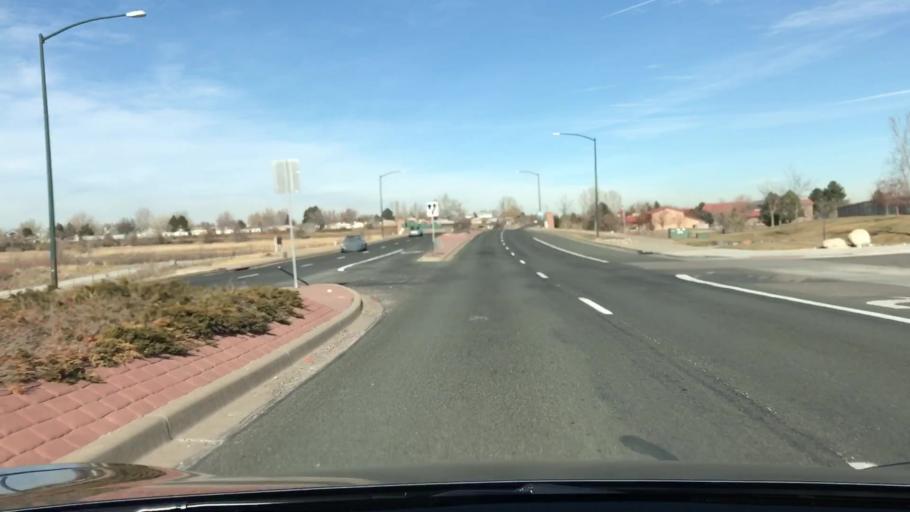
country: US
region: Colorado
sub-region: Adams County
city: Northglenn
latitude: 39.9321
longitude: -104.9969
